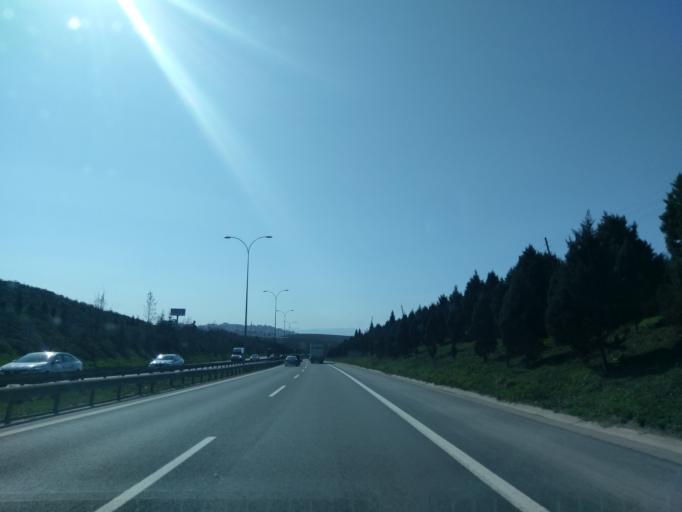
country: TR
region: Kocaeli
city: Balcik
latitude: 40.8500
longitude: 29.3746
